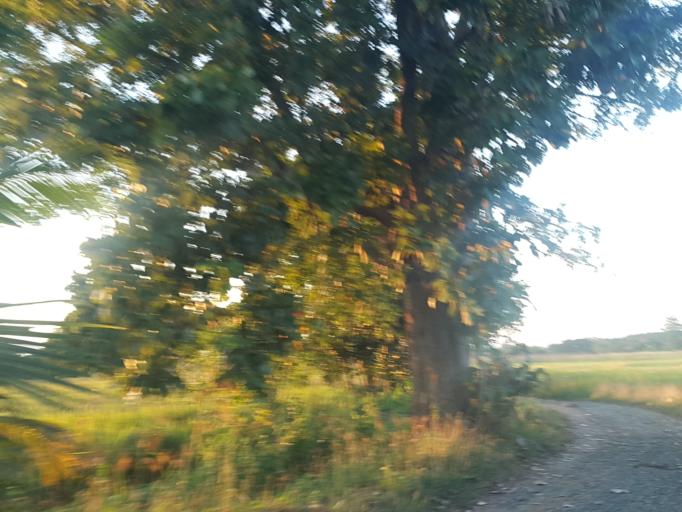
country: TH
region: Chiang Mai
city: San Kamphaeng
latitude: 18.8309
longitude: 99.1494
